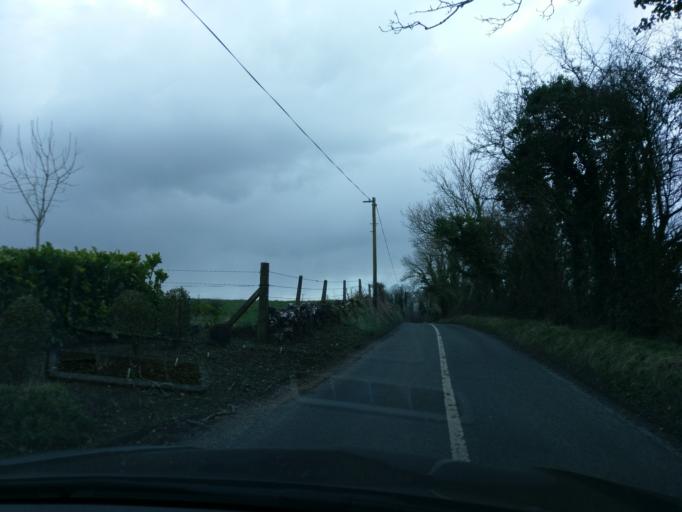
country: IE
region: Connaught
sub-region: County Galway
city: Athenry
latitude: 53.4061
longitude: -8.6359
